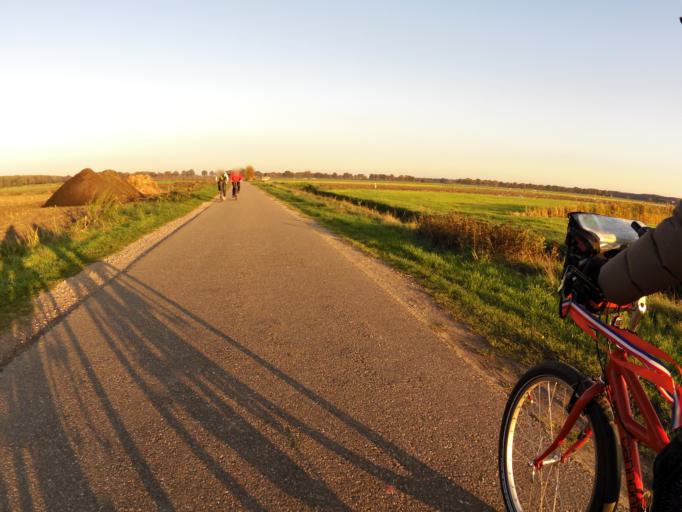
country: NL
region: North Brabant
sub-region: Gemeente Heusden
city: Heusden
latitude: 51.6798
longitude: 5.1618
